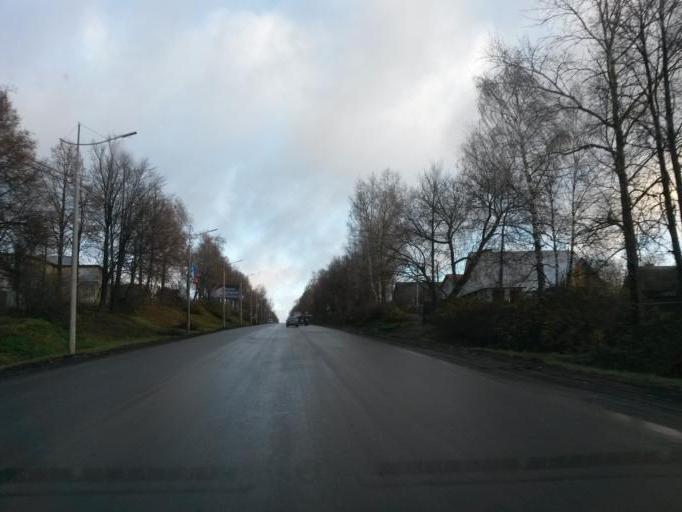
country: RU
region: Jaroslavl
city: Pereslavl'-Zalesskiy
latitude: 56.7459
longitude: 38.8581
